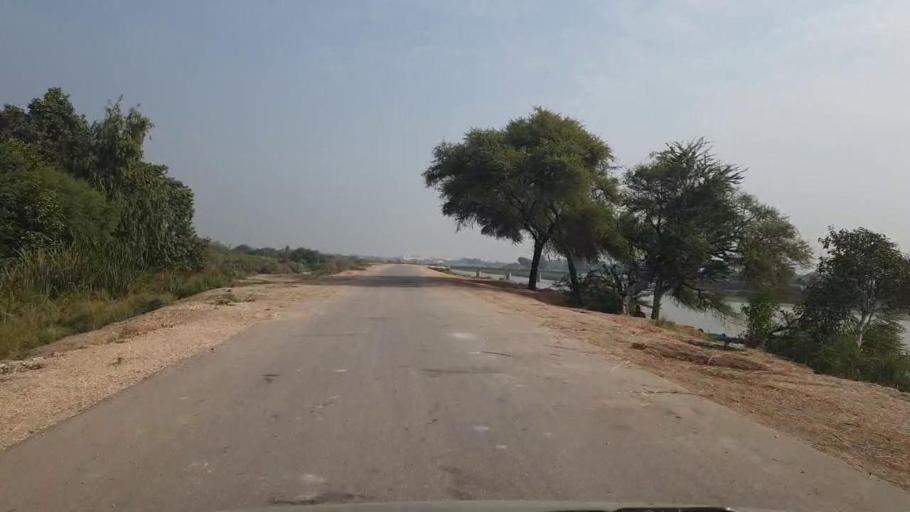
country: PK
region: Sindh
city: Tando Muhammad Khan
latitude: 25.1290
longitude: 68.5182
